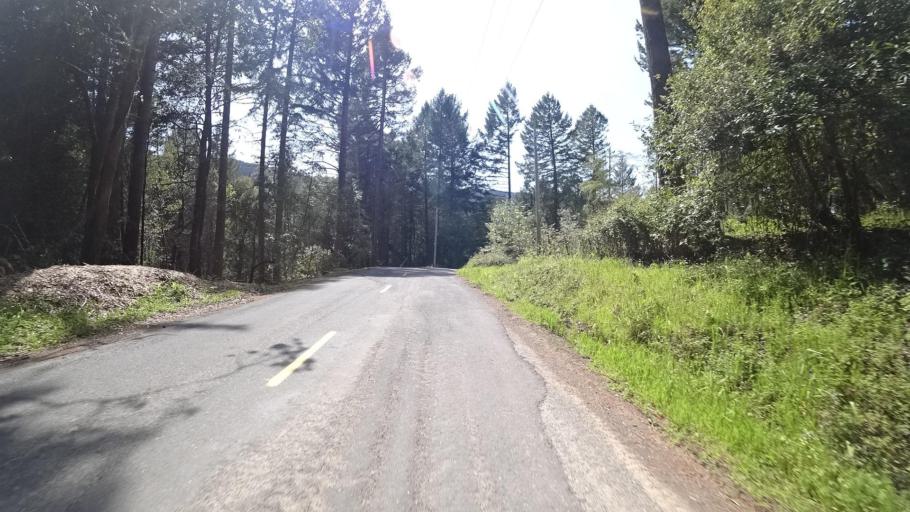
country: US
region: California
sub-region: Humboldt County
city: Redway
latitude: 40.3566
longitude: -123.7213
